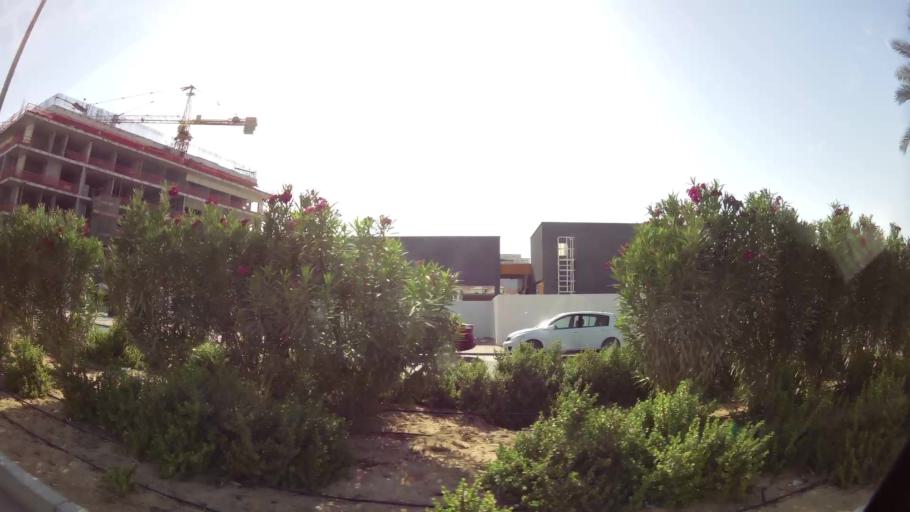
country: AE
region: Dubai
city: Dubai
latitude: 25.0551
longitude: 55.2125
